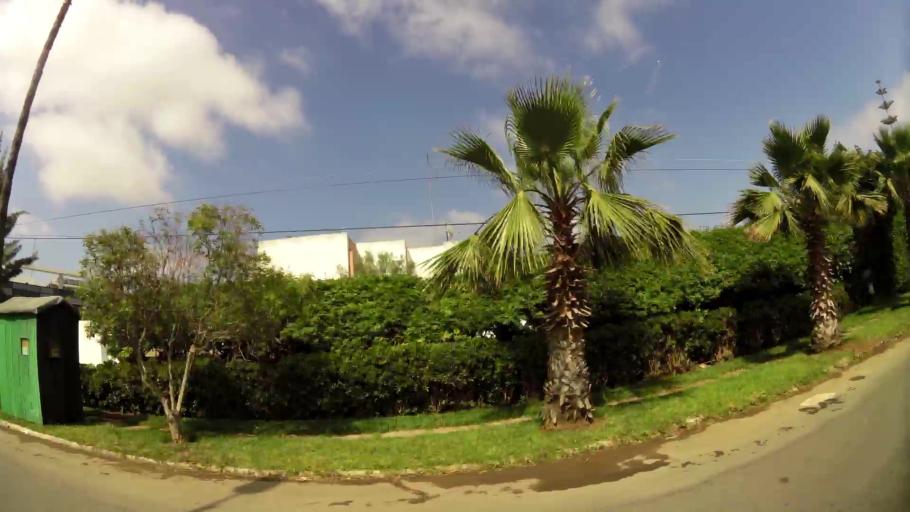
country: MA
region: Rabat-Sale-Zemmour-Zaer
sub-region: Rabat
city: Rabat
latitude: 33.9928
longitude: -6.8286
